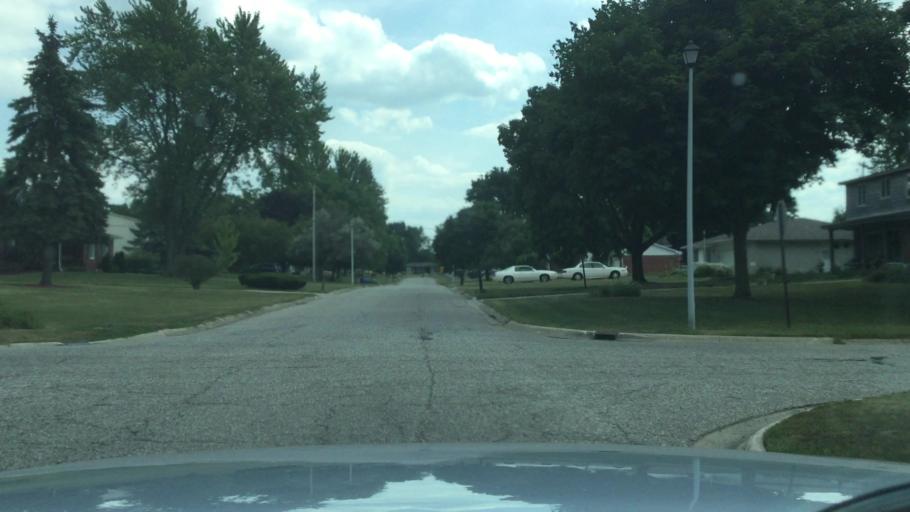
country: US
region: Michigan
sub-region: Genesee County
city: Grand Blanc
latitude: 42.9489
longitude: -83.6725
